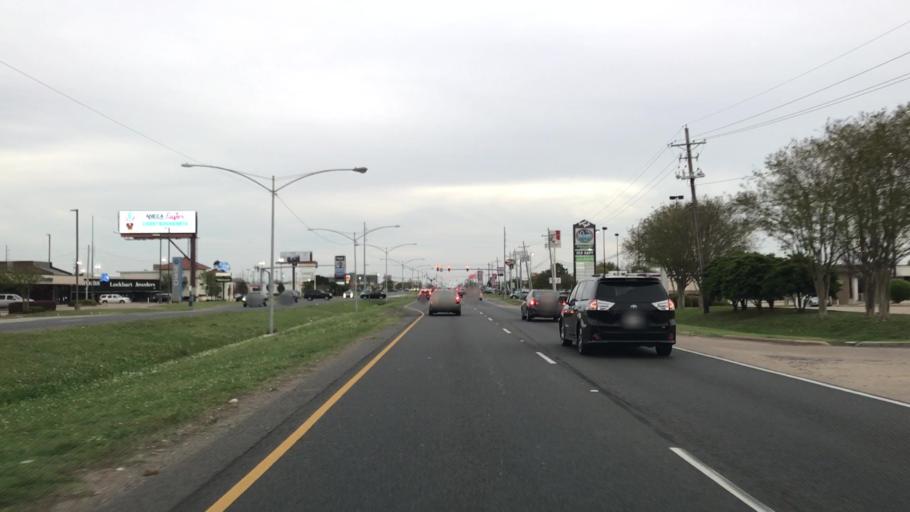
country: US
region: Louisiana
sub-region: Bossier Parish
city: Bossier City
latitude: 32.4469
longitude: -93.7207
